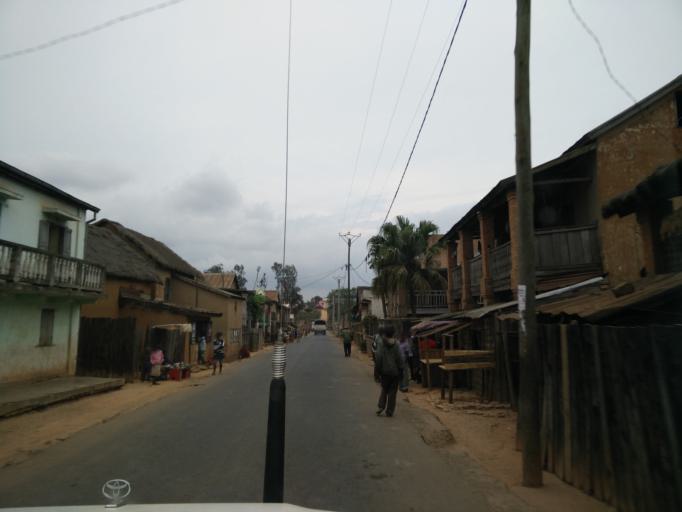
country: MG
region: Upper Matsiatra
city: Fianarantsoa
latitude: -21.5600
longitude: 47.0391
